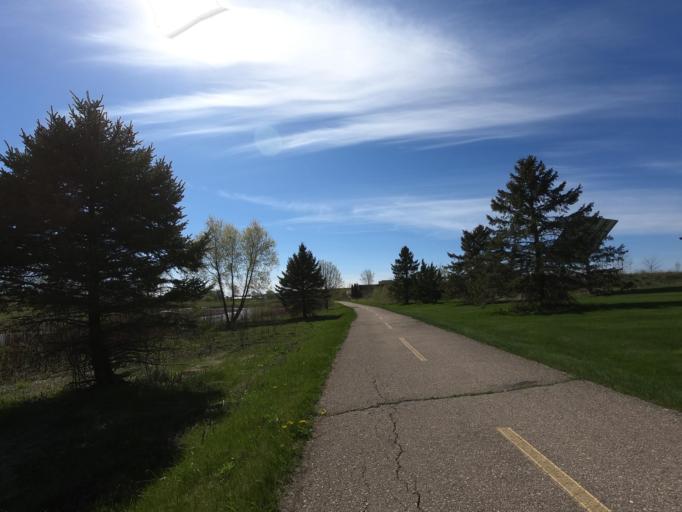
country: US
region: Wisconsin
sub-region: Dane County
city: Middleton
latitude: 43.1050
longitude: -89.5225
